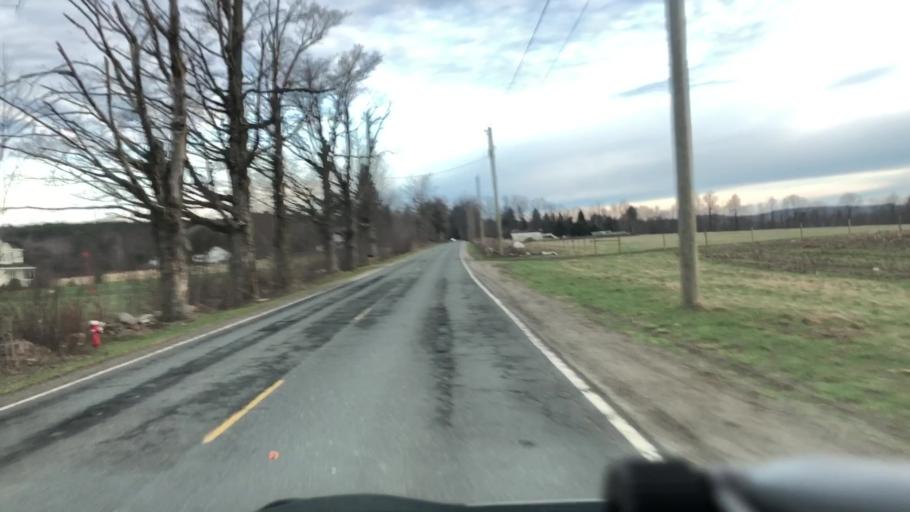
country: US
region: Massachusetts
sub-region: Hampshire County
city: Chesterfield
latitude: 42.4154
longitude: -72.9385
